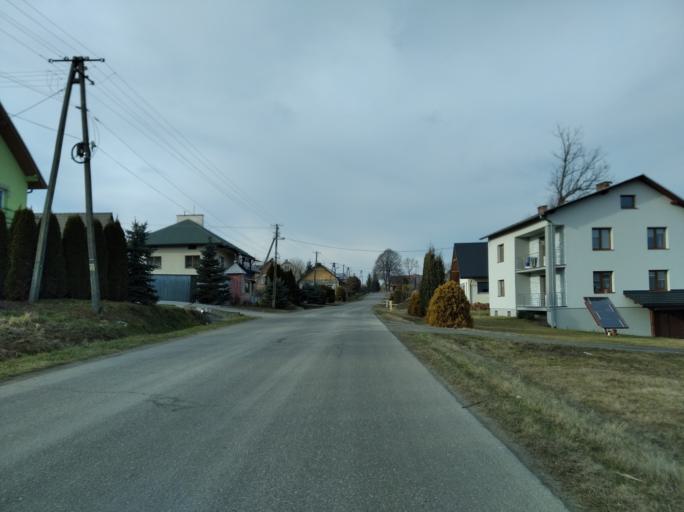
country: PL
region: Subcarpathian Voivodeship
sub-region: Powiat brzozowski
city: Stara Wies
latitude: 49.7313
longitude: 21.9859
